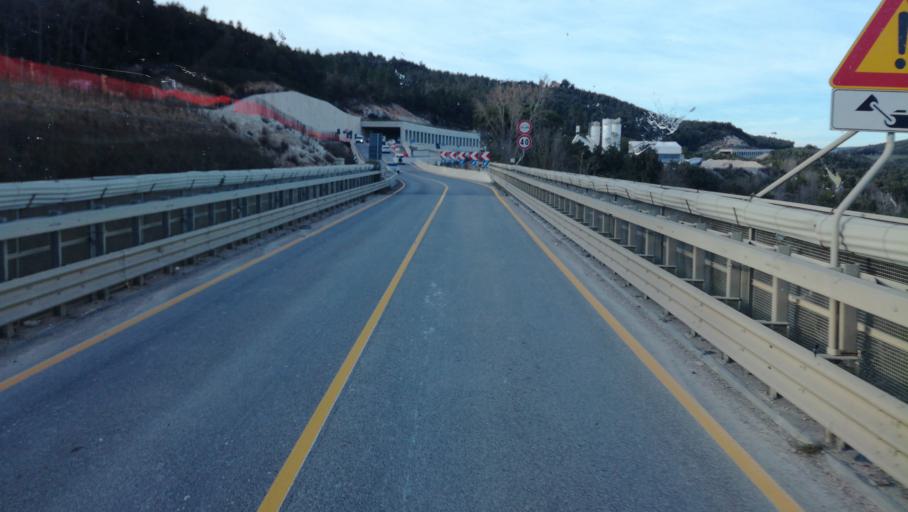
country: IT
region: Tuscany
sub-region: Provincia di Grosseto
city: Civitella Marittima
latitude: 43.0766
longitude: 11.2967
